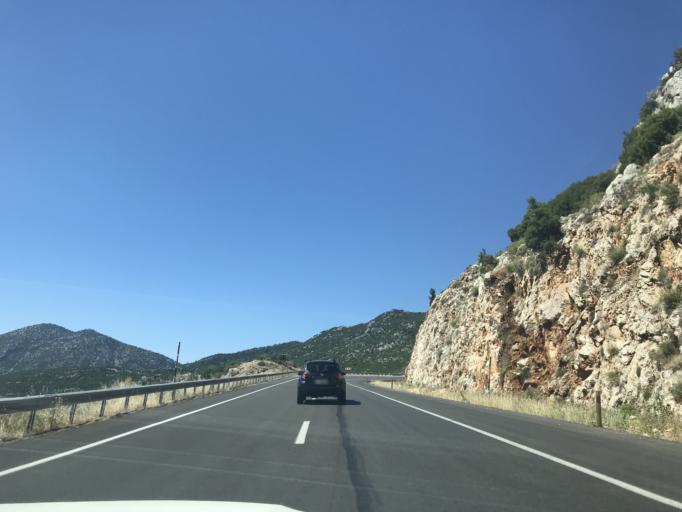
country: TR
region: Antalya
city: Dagbeli
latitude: 37.1643
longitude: 30.5091
